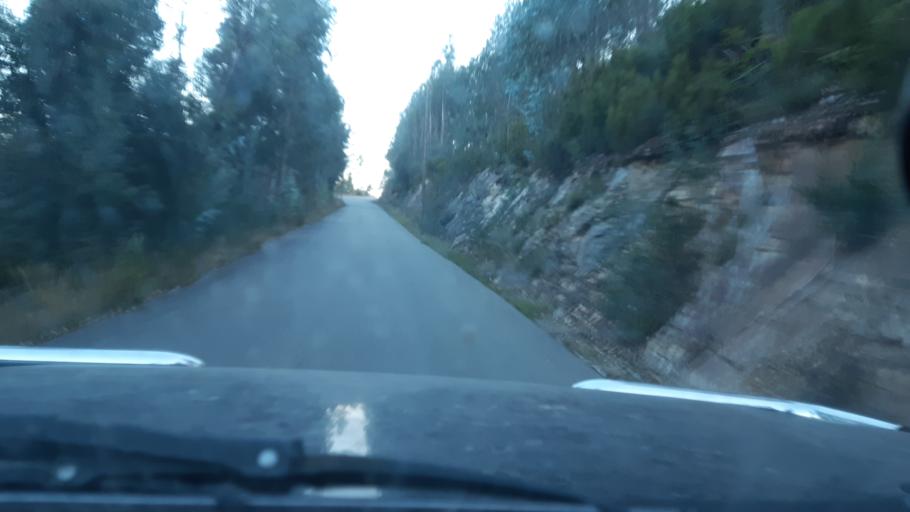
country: PT
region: Aveiro
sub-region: Agueda
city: Aguada de Cima
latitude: 40.5678
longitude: -8.3618
